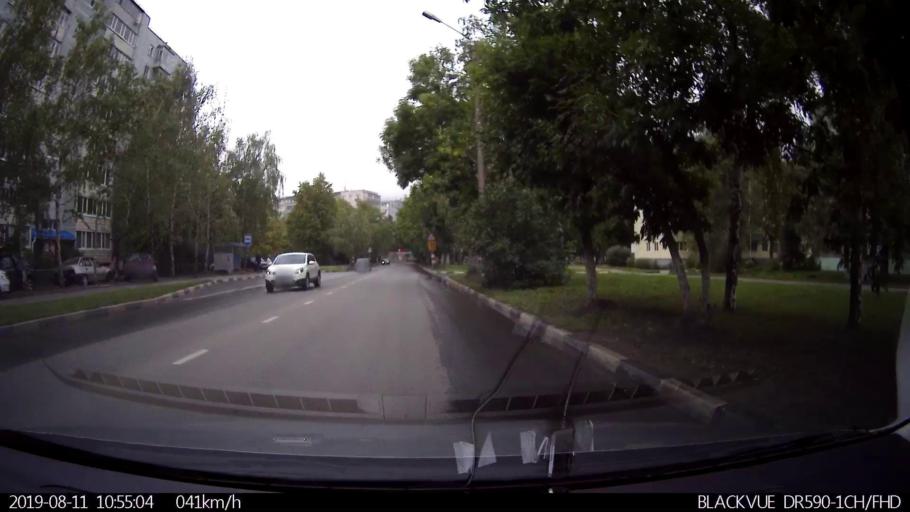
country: RU
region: Ulyanovsk
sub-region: Ulyanovskiy Rayon
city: Ulyanovsk
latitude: 54.2556
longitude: 48.3317
